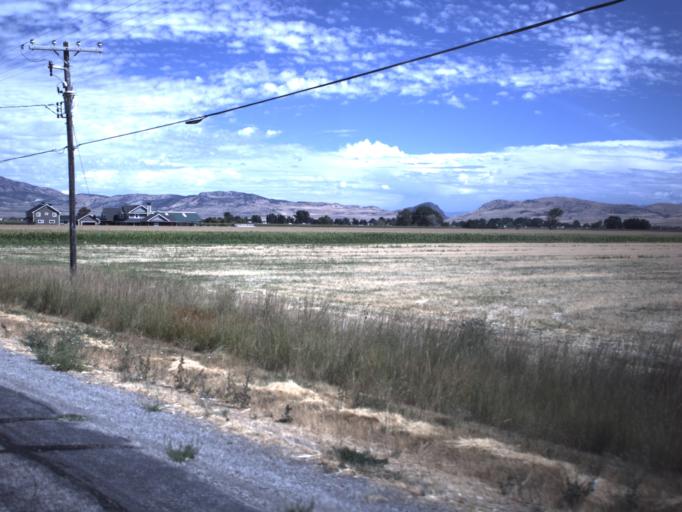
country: US
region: Utah
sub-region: Box Elder County
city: Garland
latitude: 41.7560
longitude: -112.1484
